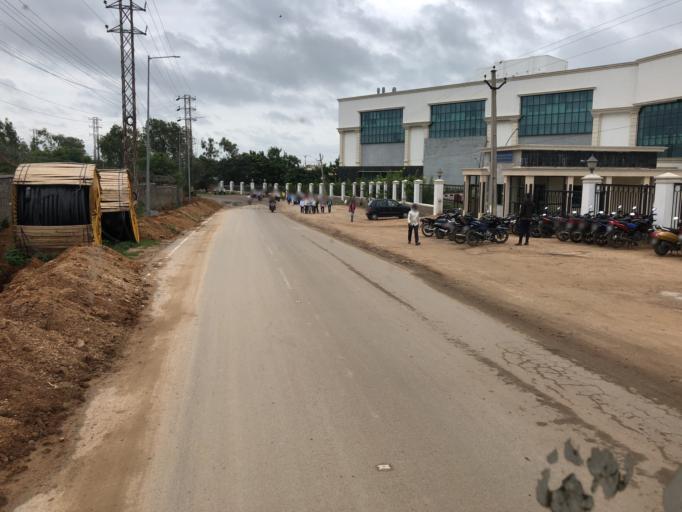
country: IN
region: Telangana
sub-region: Medak
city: Serilingampalle
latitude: 17.4446
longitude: 78.3055
